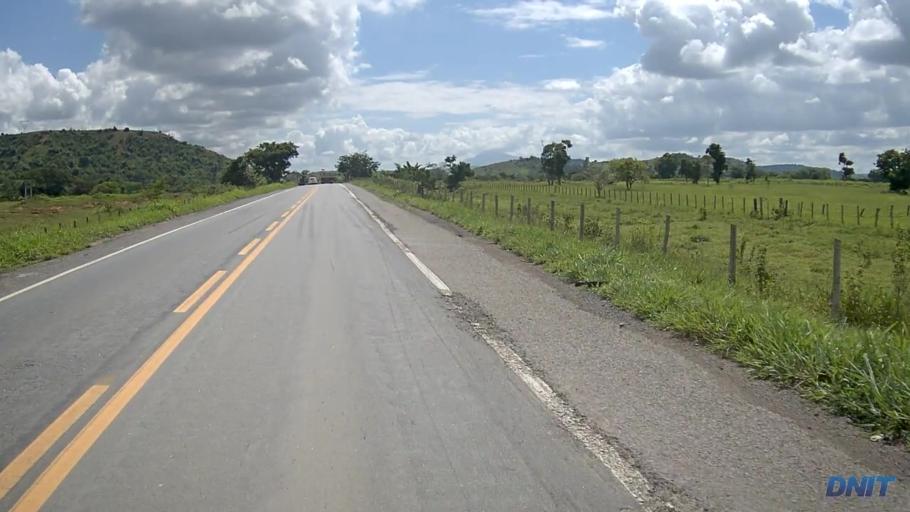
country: BR
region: Minas Gerais
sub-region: Governador Valadares
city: Governador Valadares
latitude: -19.0033
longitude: -42.1285
